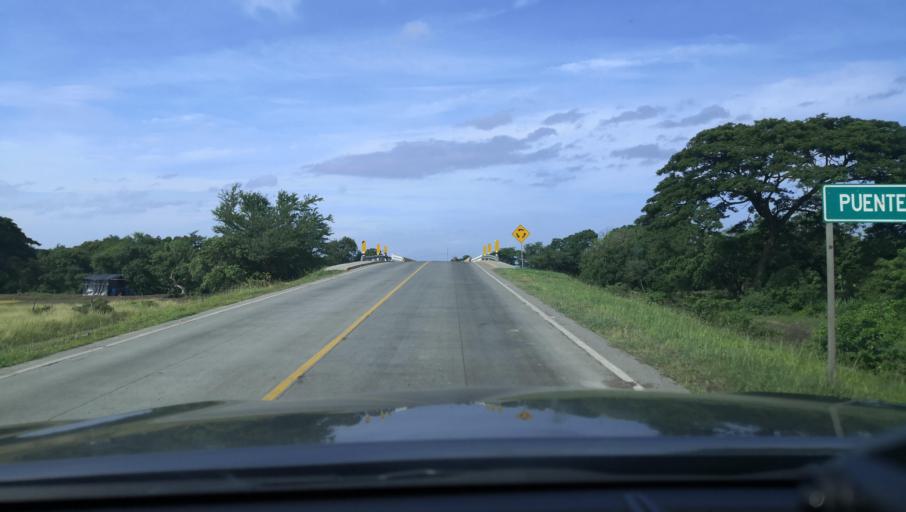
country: NI
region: Masaya
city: Tisma
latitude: 12.1540
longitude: -85.8448
